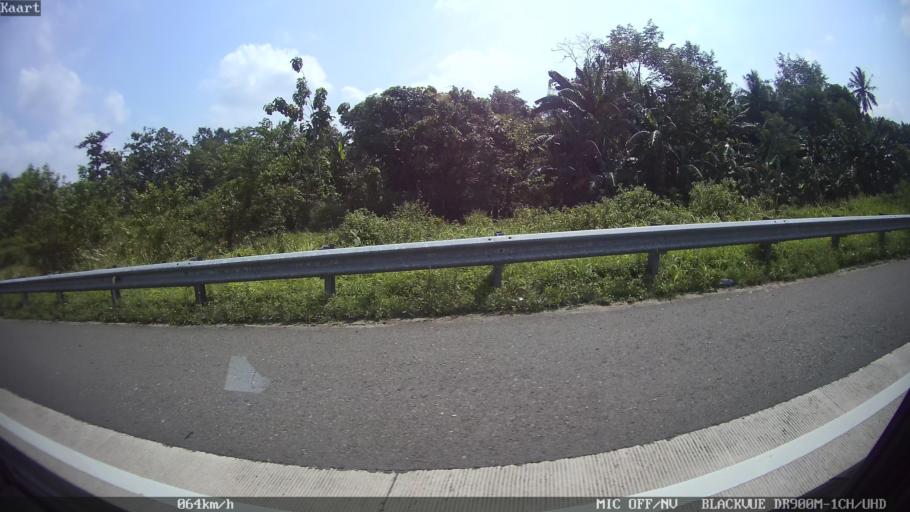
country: ID
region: Lampung
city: Natar
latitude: -5.3121
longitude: 105.2539
